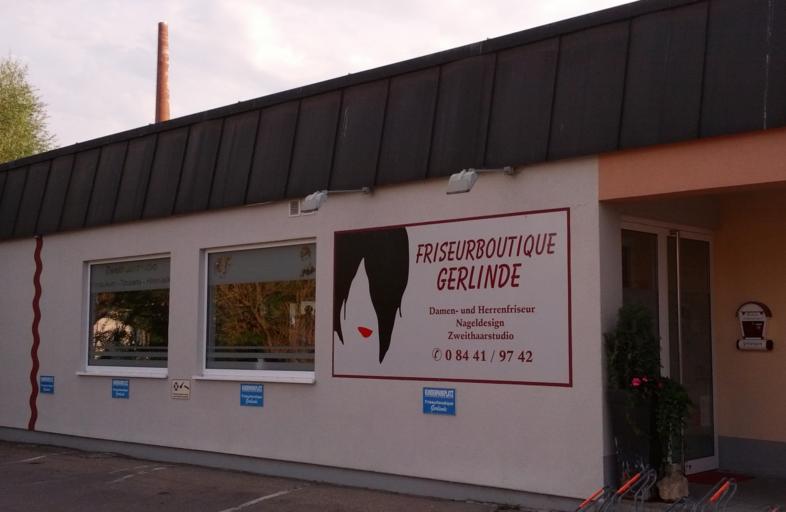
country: DE
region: Bavaria
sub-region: Upper Bavaria
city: Pfaffenhofen an der Ilm
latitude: 48.5282
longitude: 11.5076
